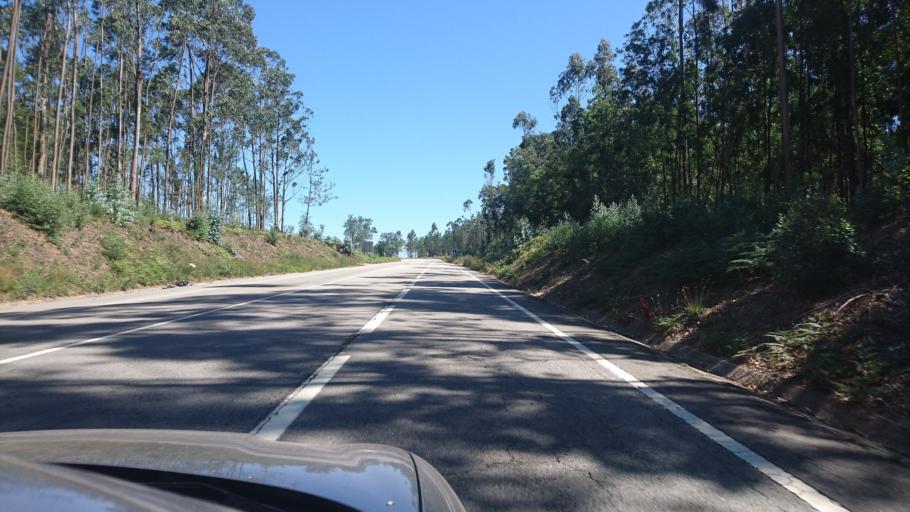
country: PT
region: Aveiro
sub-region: Santa Maria da Feira
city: Rio Meao
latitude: 40.9353
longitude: -8.5825
